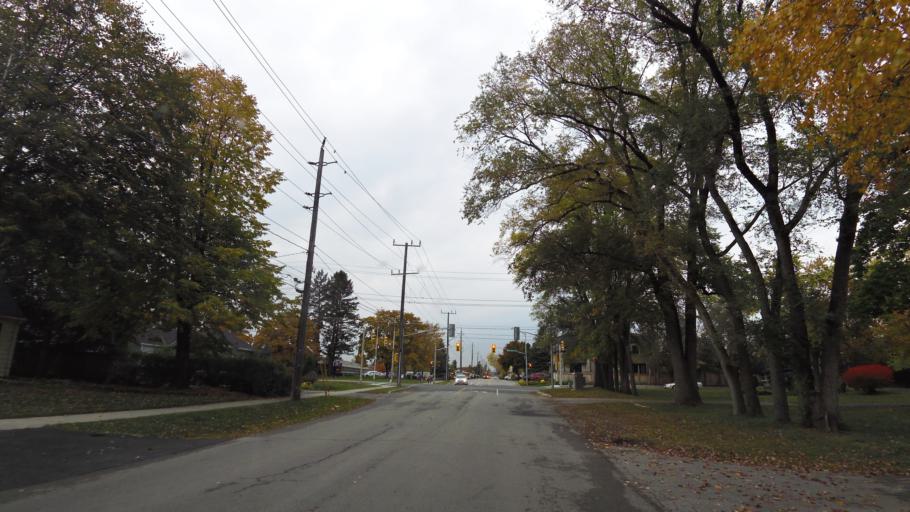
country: CA
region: Ontario
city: Oakville
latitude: 43.4336
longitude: -79.6844
